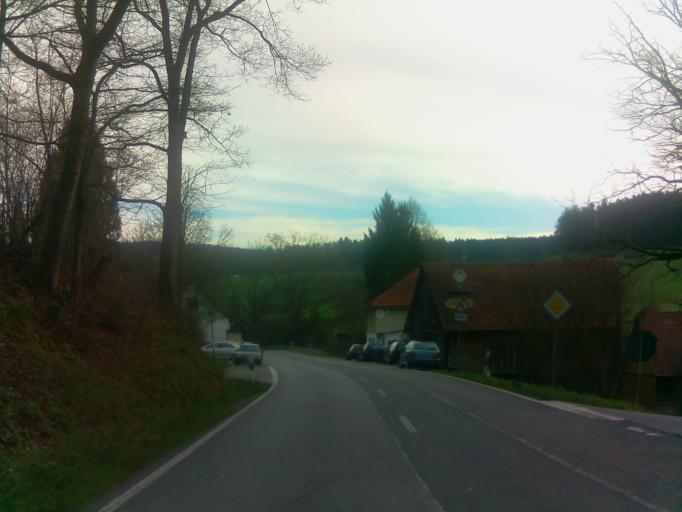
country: DE
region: Hesse
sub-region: Regierungsbezirk Darmstadt
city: Beerfelden
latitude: 49.6249
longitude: 8.9215
